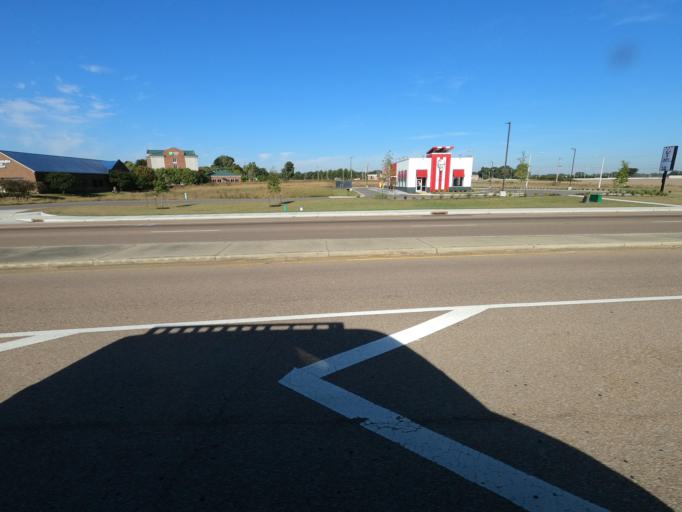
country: US
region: Tennessee
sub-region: Shelby County
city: Millington
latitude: 35.3616
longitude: -89.8913
